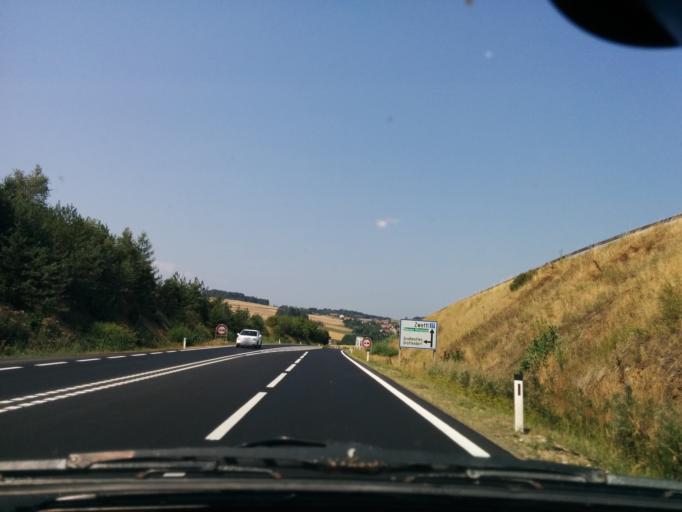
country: AT
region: Lower Austria
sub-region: Politischer Bezirk Krems
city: Krumau am Kamp
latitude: 48.5317
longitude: 15.4115
